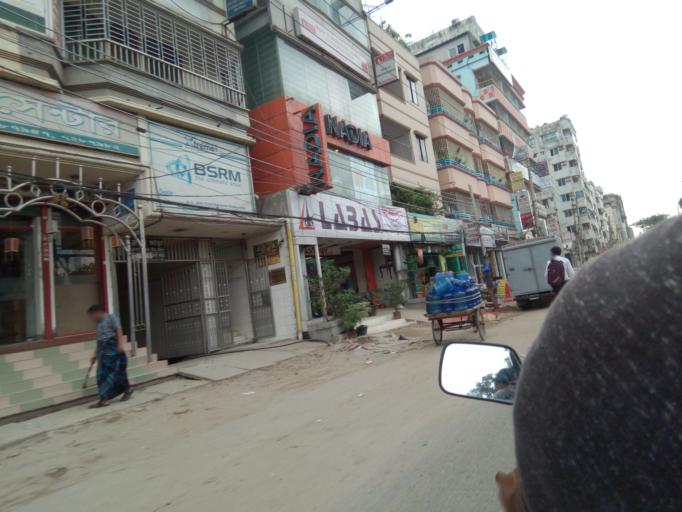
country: BD
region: Dhaka
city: Paltan
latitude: 23.7649
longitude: 90.4287
